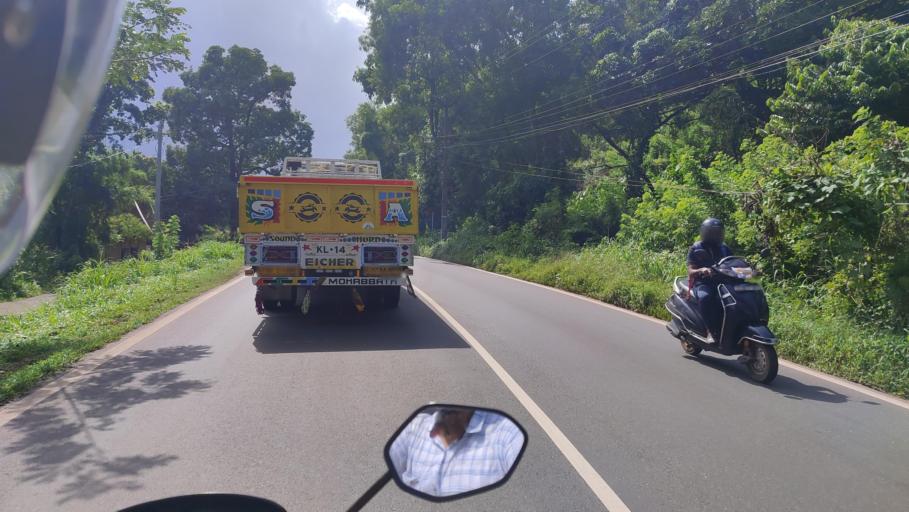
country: IN
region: Kerala
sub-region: Kasaragod District
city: Nileshwar
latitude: 12.2196
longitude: 75.1620
